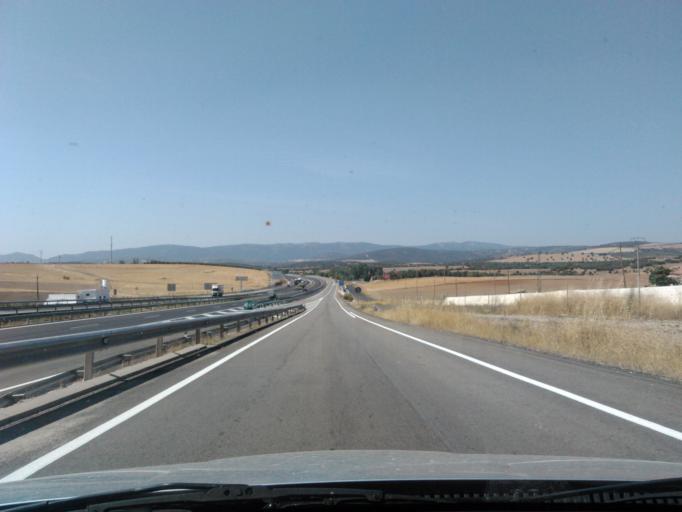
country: ES
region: Castille-La Mancha
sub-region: Provincia de Ciudad Real
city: Viso del Marques
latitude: 38.5045
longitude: -3.4999
